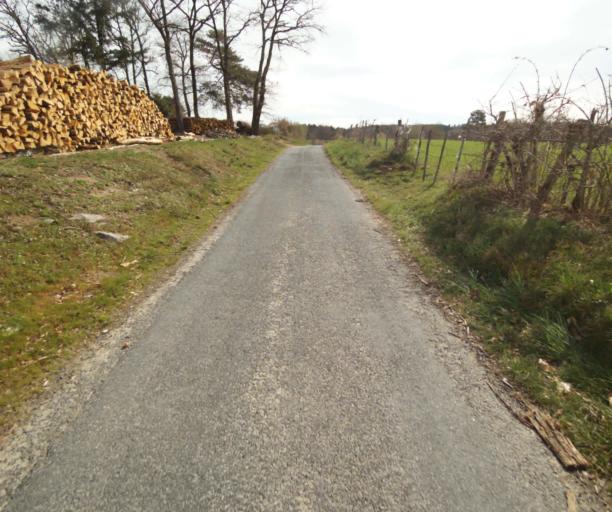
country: FR
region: Limousin
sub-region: Departement de la Correze
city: Correze
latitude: 45.3685
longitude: 1.8988
